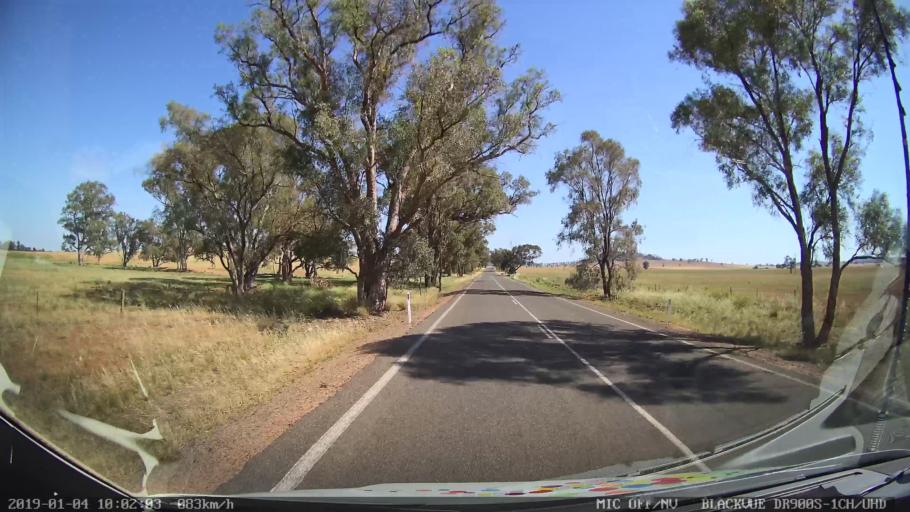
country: AU
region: New South Wales
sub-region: Cabonne
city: Canowindra
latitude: -33.4811
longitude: 148.3662
